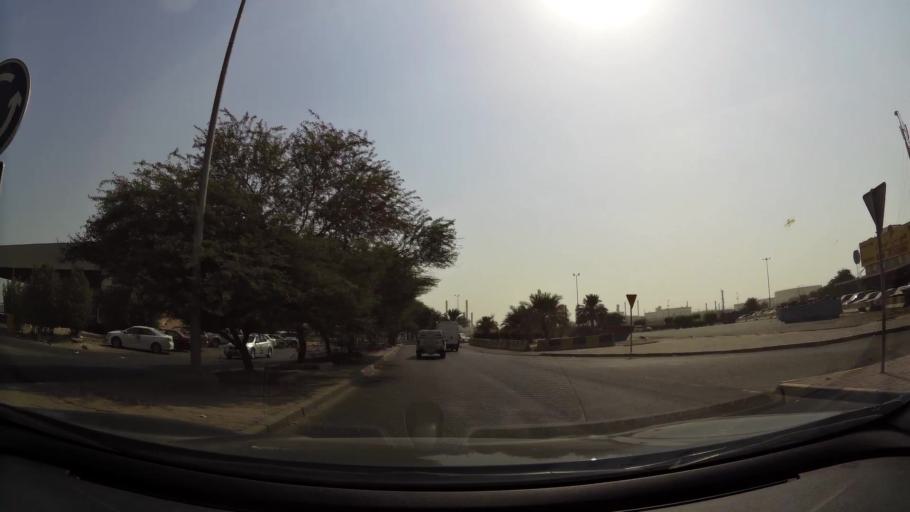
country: KW
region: Al Ahmadi
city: Al Fahahil
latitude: 29.0712
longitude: 48.1259
